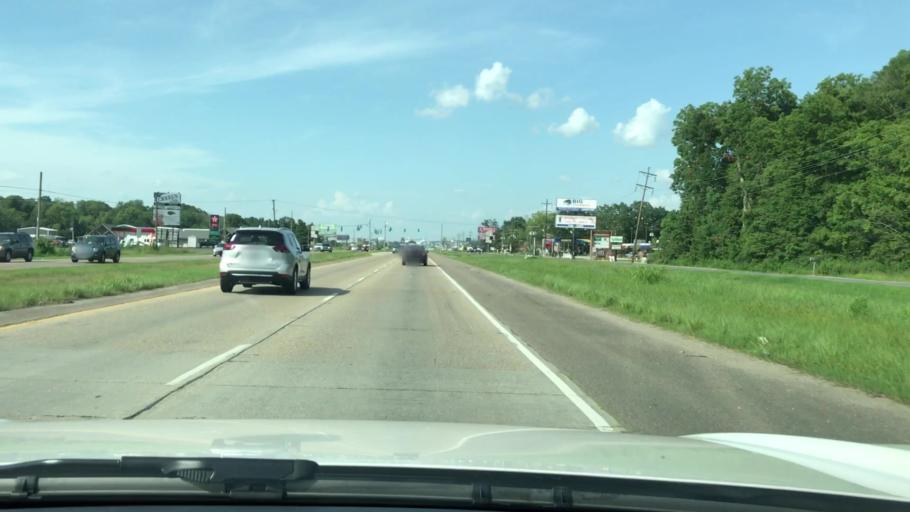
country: US
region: Louisiana
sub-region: West Baton Rouge Parish
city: Brusly
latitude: 30.4126
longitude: -91.2257
